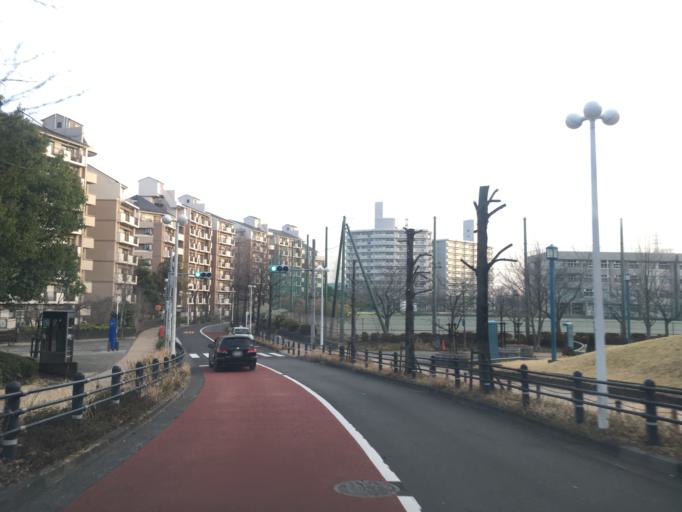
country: JP
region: Tokyo
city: Hino
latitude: 35.6179
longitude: 139.3996
